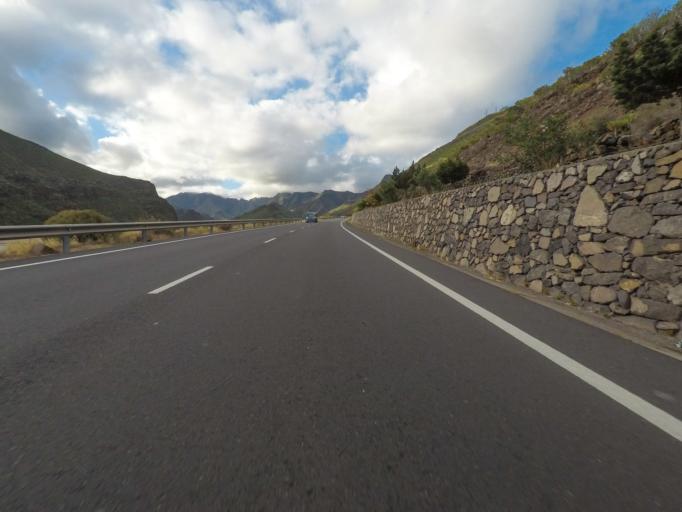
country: ES
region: Canary Islands
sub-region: Provincia de Santa Cruz de Tenerife
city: San Sebastian de la Gomera
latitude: 28.0986
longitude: -17.1169
